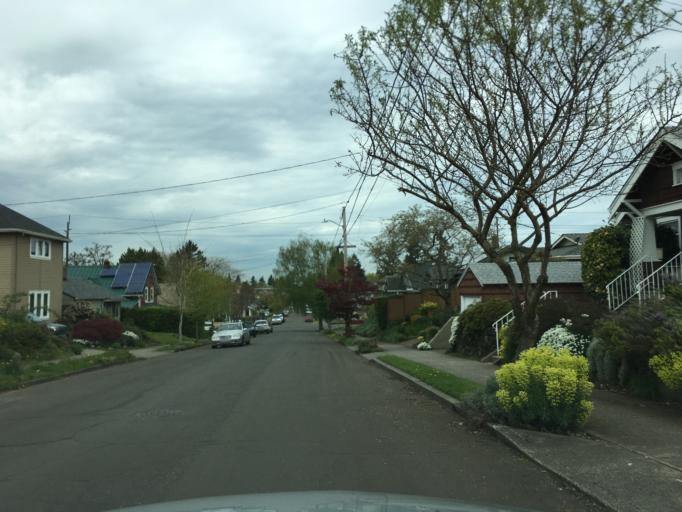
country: US
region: Oregon
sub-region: Multnomah County
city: Lents
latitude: 45.5217
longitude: -122.5858
